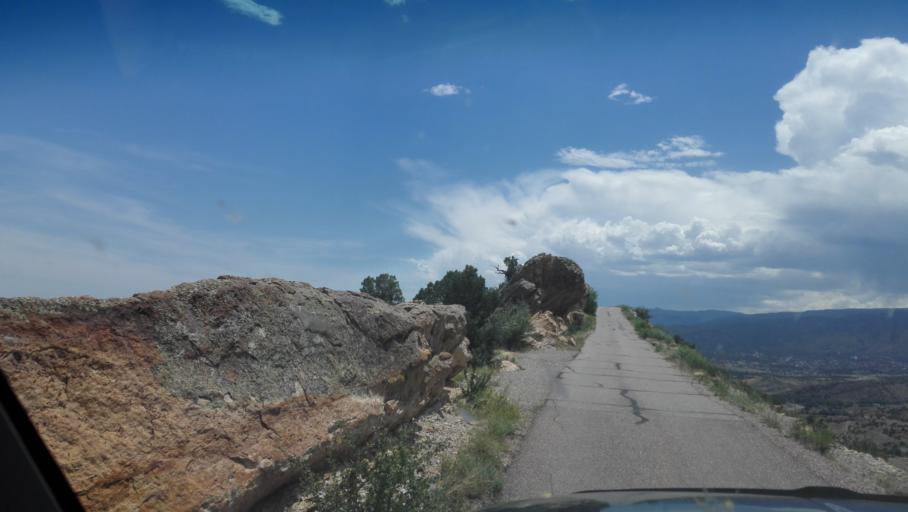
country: US
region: Colorado
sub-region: Fremont County
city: Canon City
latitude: 38.4609
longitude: -105.2512
